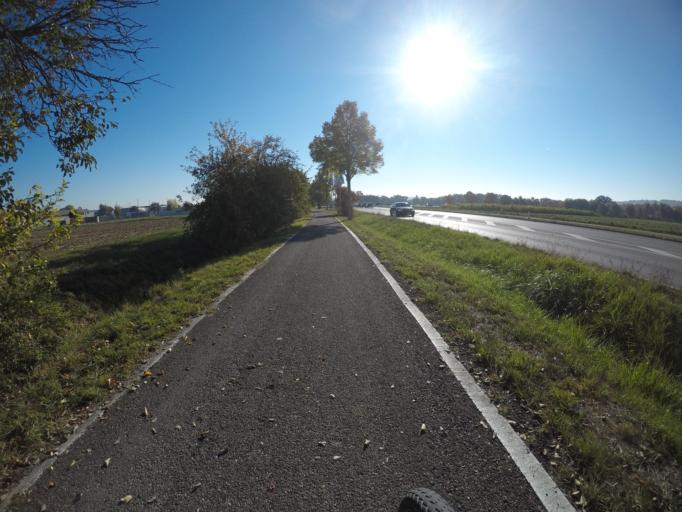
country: DE
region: Baden-Wuerttemberg
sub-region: Regierungsbezirk Stuttgart
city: Leinfelden-Echterdingen
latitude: 48.6789
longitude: 9.1875
